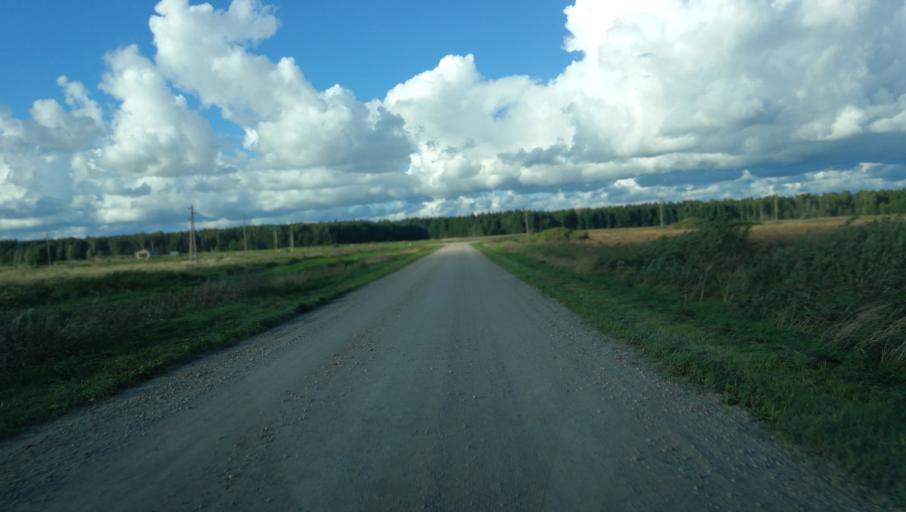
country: LV
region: Carnikava
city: Carnikava
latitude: 57.0818
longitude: 24.2283
